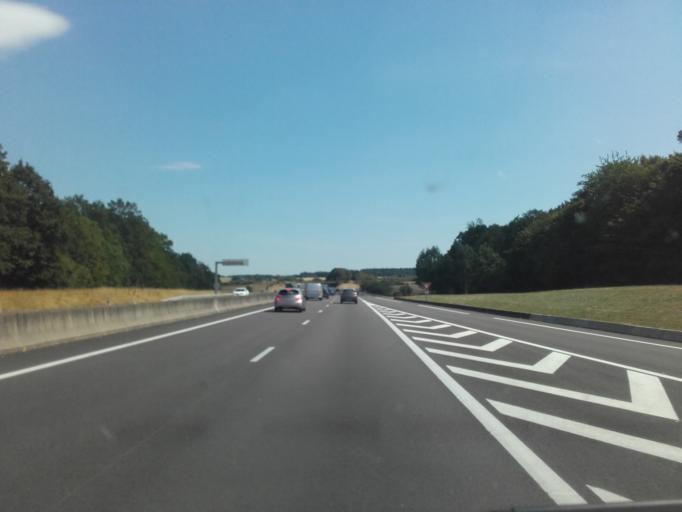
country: FR
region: Bourgogne
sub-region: Departement de la Cote-d'Or
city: Semur-en-Auxois
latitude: 47.3872
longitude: 4.3679
